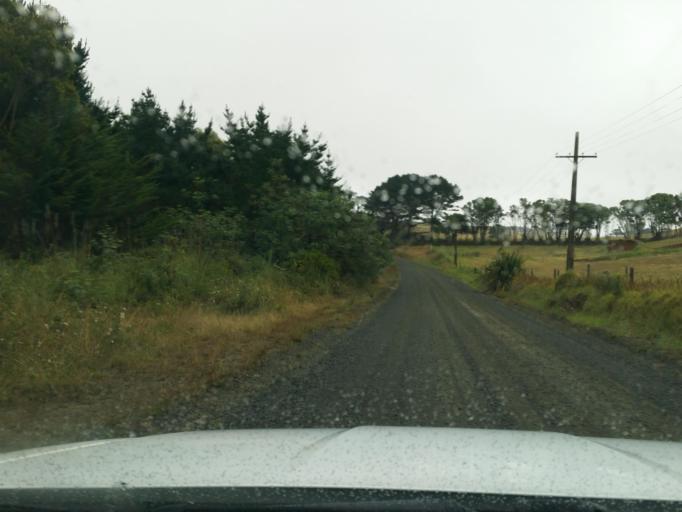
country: NZ
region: Northland
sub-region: Kaipara District
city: Dargaville
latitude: -36.0767
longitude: 173.8851
